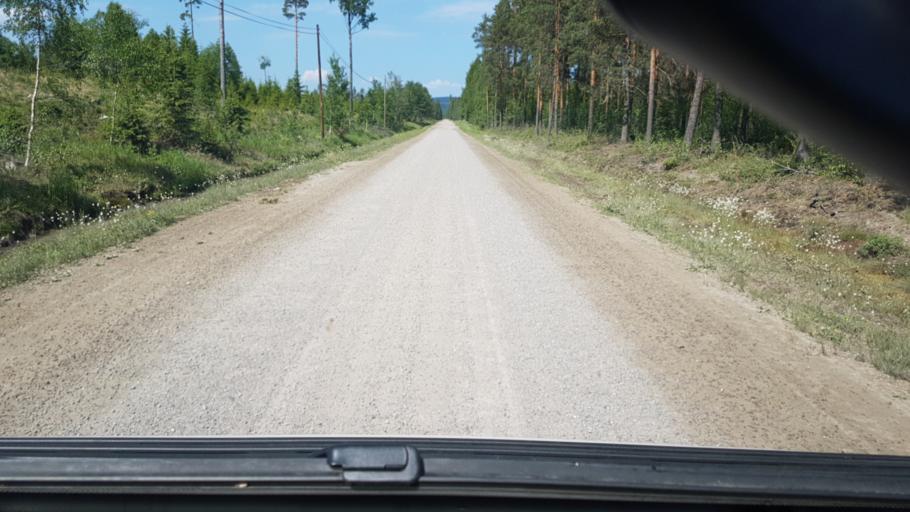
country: SE
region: Vaermland
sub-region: Eda Kommun
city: Charlottenberg
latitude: 59.9507
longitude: 12.5165
